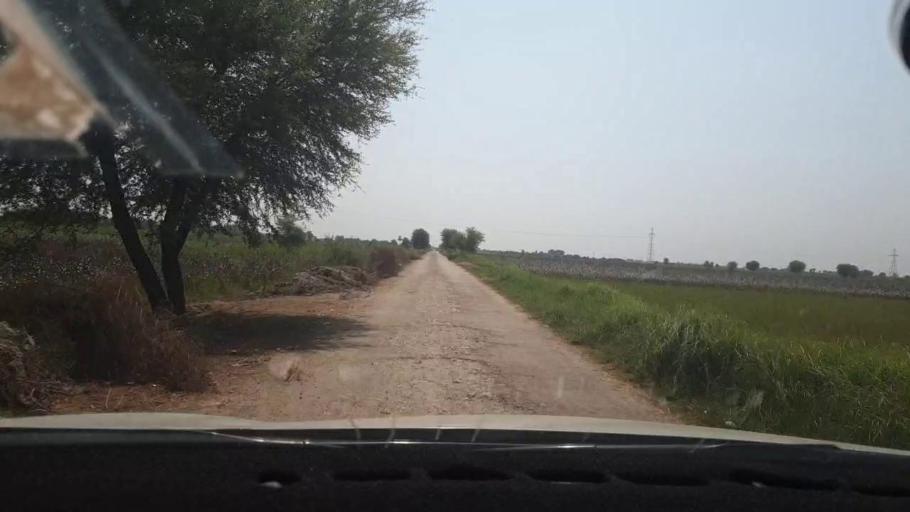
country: PK
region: Sindh
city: Tando Mittha Khan
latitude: 25.9057
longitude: 69.2066
